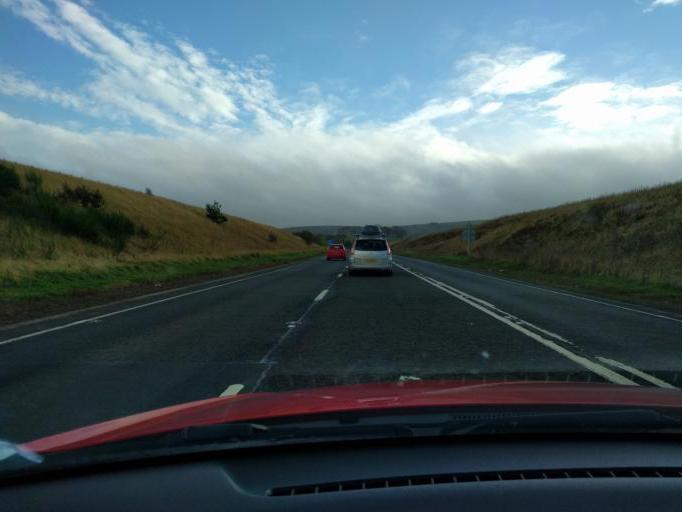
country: GB
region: Scotland
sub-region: The Scottish Borders
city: Duns
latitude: 55.9303
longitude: -2.3552
